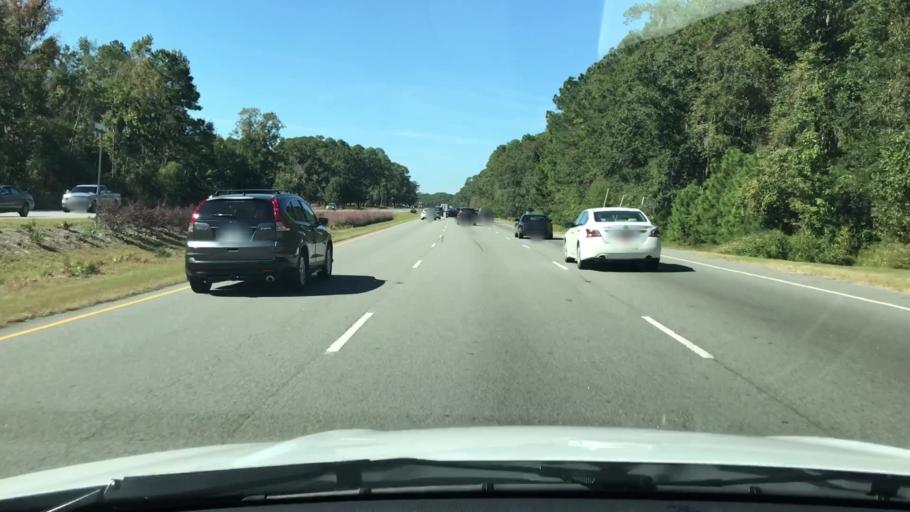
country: US
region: South Carolina
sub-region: Beaufort County
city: Bluffton
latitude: 32.2813
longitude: -80.8760
